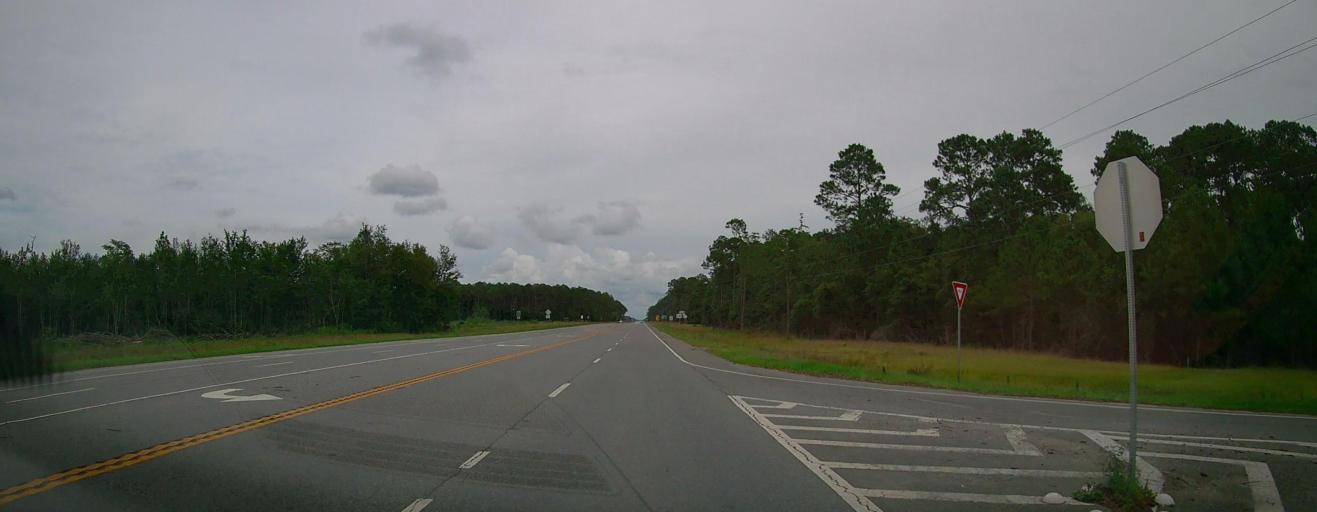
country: US
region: Georgia
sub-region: Appling County
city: Baxley
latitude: 31.7662
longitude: -82.3132
